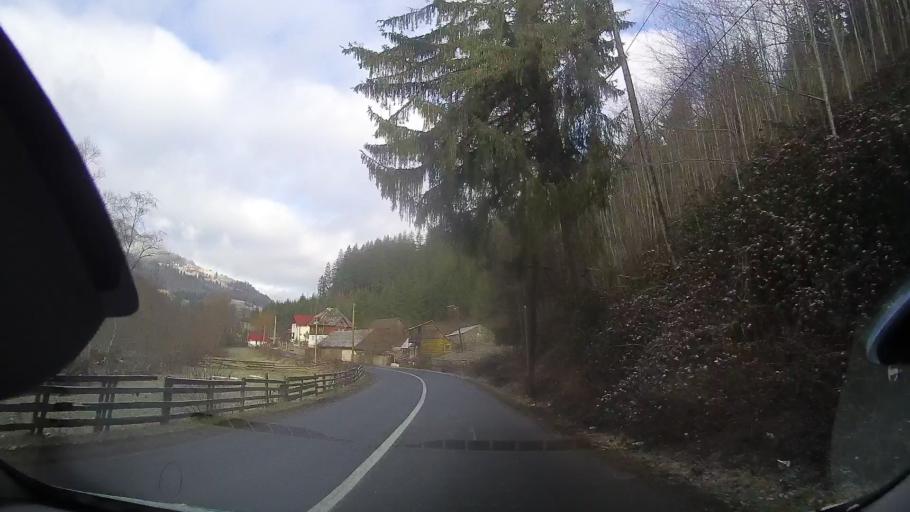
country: RO
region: Alba
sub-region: Comuna Albac
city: Albac
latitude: 46.4593
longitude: 22.9754
